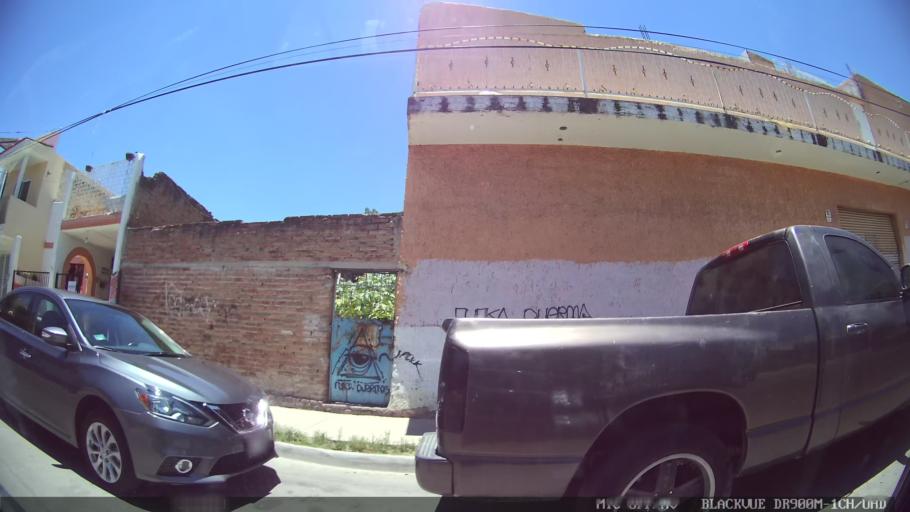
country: MX
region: Jalisco
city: Tlaquepaque
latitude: 20.6758
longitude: -103.2917
